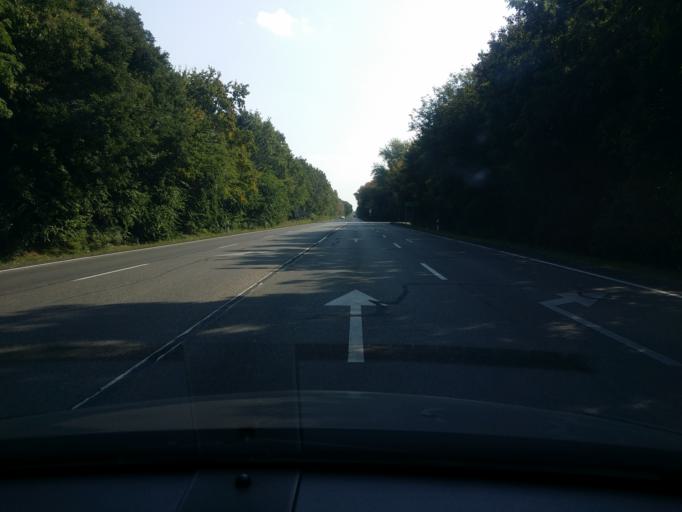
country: HU
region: Fejer
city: dunaujvaros
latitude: 46.9408
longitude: 18.9185
